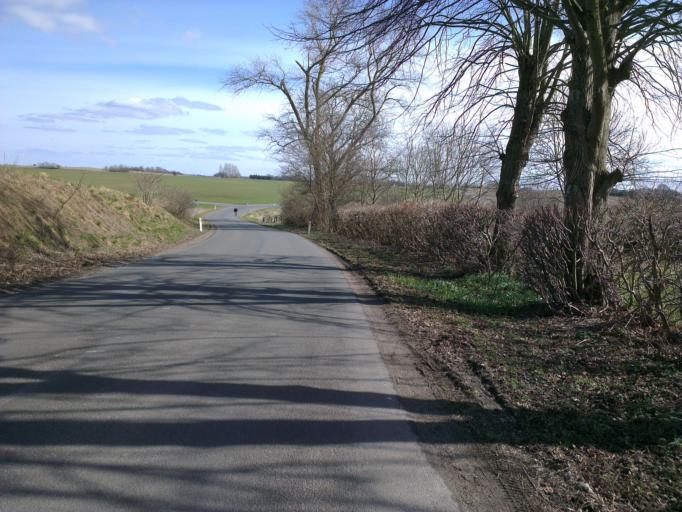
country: DK
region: Capital Region
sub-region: Frederikssund Kommune
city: Skibby
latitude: 55.7424
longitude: 12.0115
